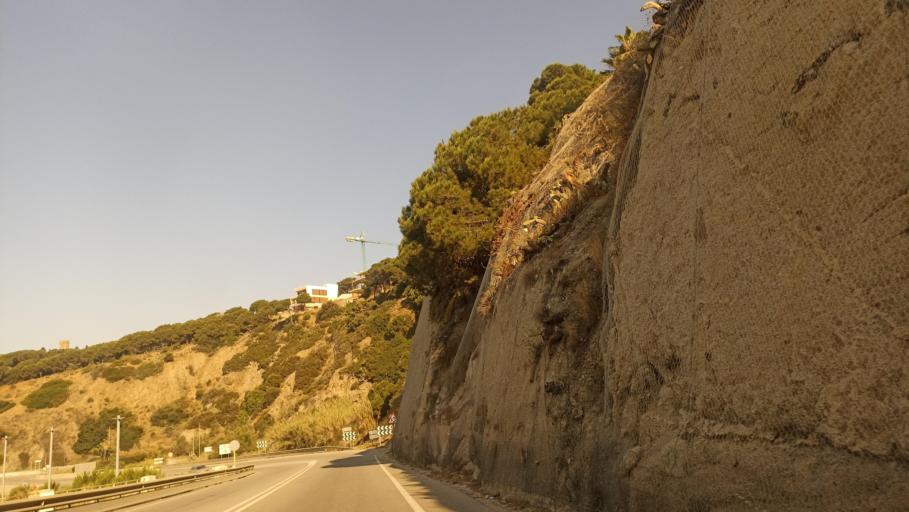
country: ES
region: Catalonia
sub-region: Provincia de Barcelona
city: Caldes d'Estrac
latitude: 41.5728
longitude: 2.5377
